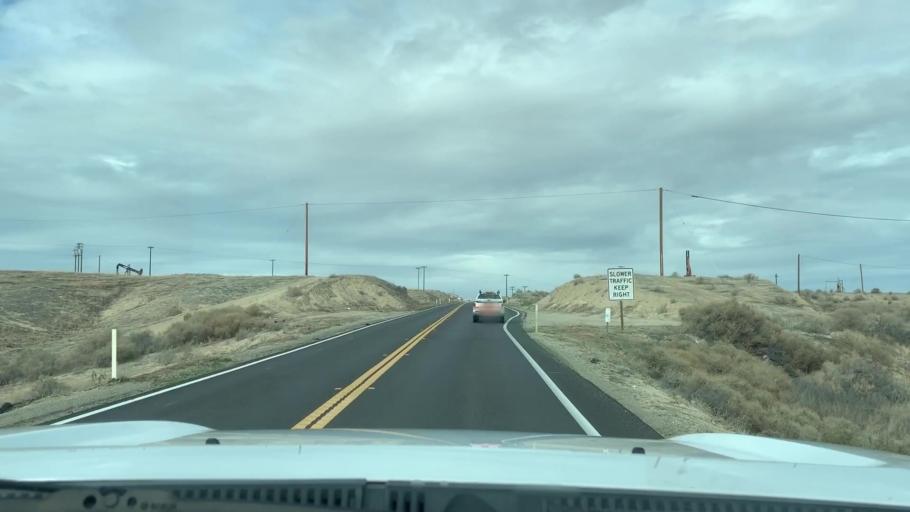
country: US
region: California
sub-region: Kern County
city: South Taft
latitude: 35.1132
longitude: -119.4277
